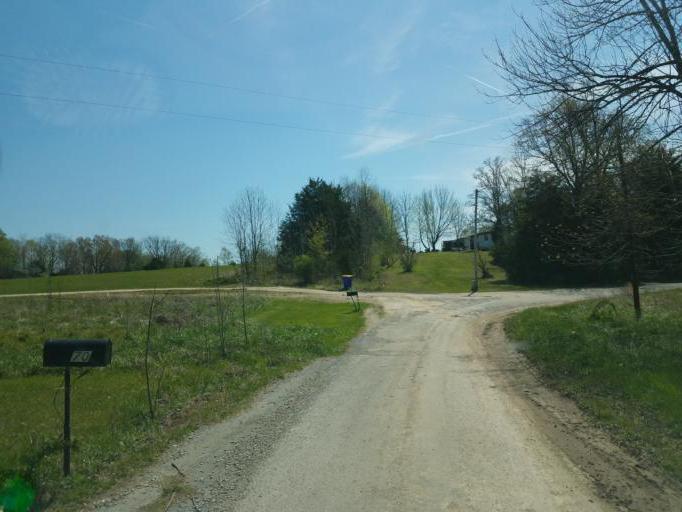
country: US
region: Kentucky
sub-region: Barren County
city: Cave City
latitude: 37.1455
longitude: -86.0376
